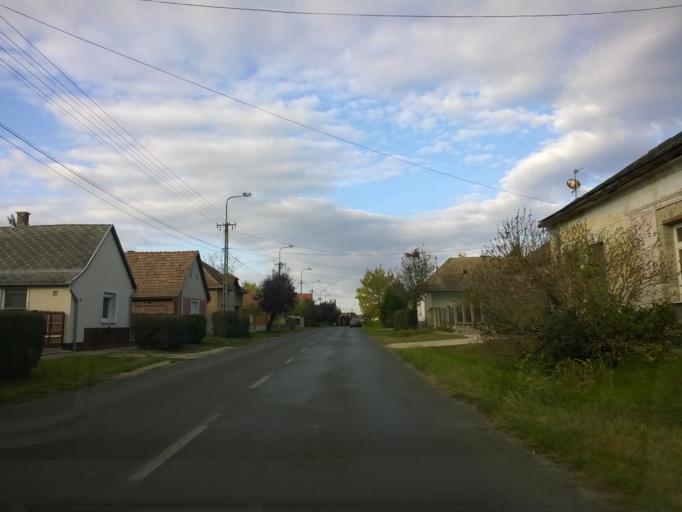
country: HU
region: Pest
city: Szigetujfalu
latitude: 47.2337
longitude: 18.9593
